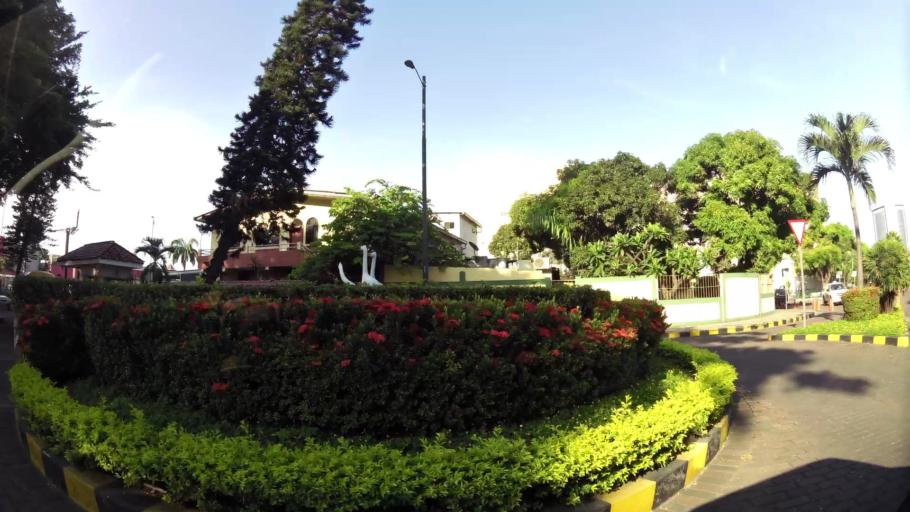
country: EC
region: Guayas
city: Guayaquil
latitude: -2.1681
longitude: -79.8973
